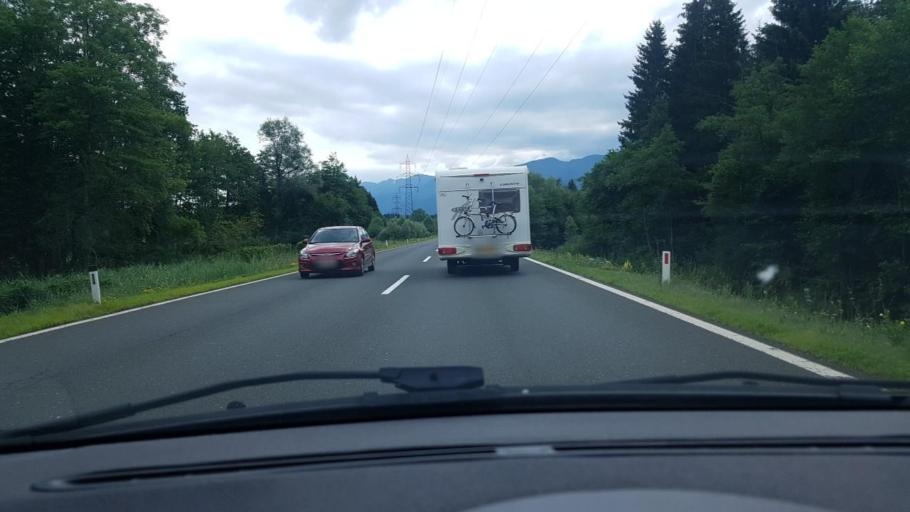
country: AT
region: Carinthia
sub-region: Politischer Bezirk Villach Land
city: Hohenthurn
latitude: 46.5708
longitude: 13.6501
